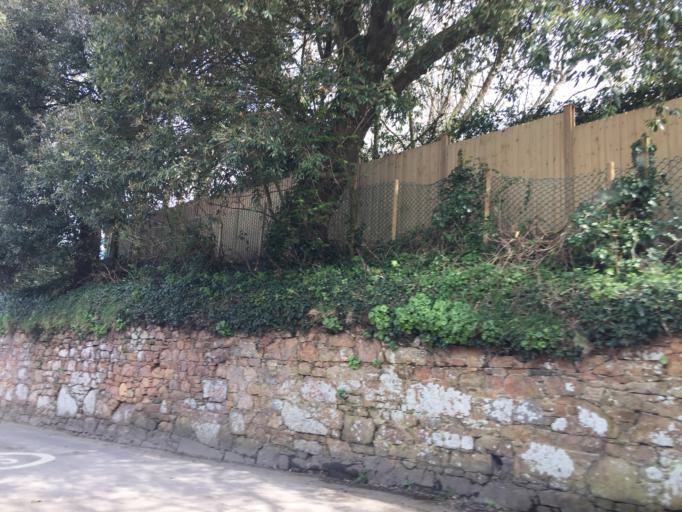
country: JE
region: St Helier
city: Saint Helier
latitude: 49.2380
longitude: -2.1818
